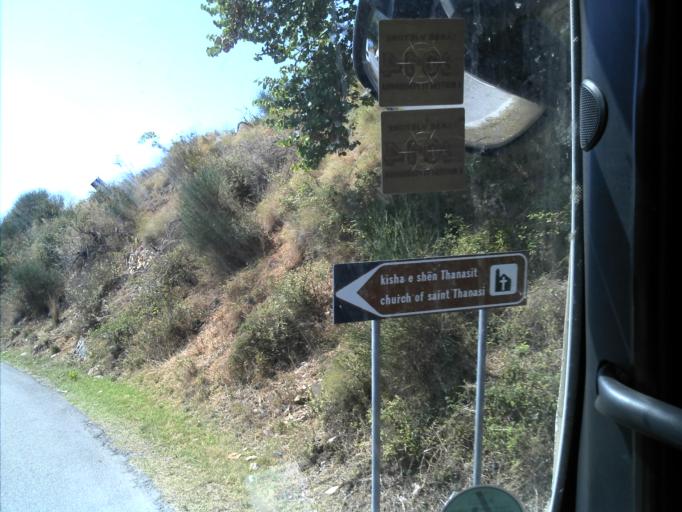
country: AL
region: Gjirokaster
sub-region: Rrethi i Gjirokastres
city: Dervician
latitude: 39.9339
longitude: 20.2044
